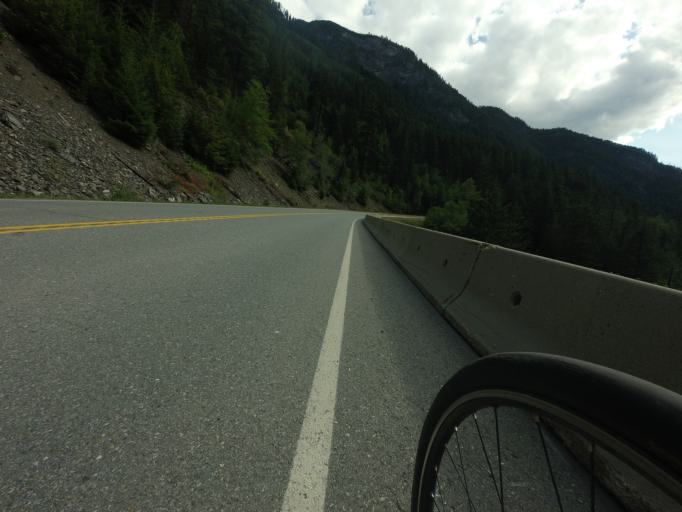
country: CA
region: British Columbia
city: Lillooet
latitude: 50.6427
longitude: -122.0687
